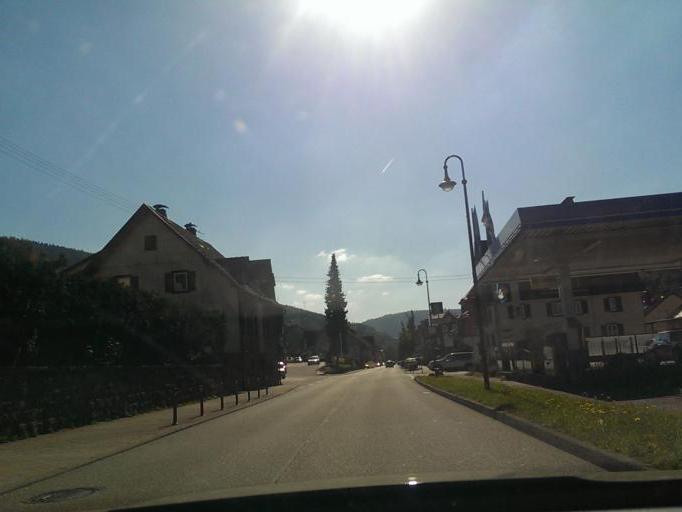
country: DE
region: Baden-Wuerttemberg
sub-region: Karlsruhe Region
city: Hofen an der Enz
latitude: 48.8080
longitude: 8.5842
